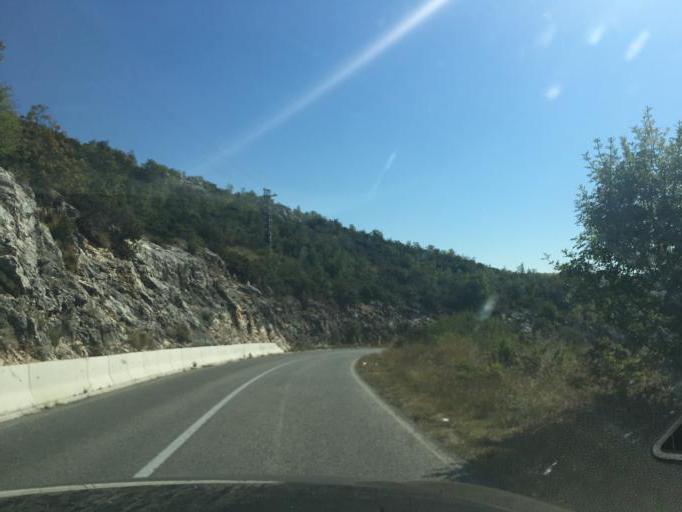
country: HR
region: Splitsko-Dalmatinska
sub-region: Grad Trogir
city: Trogir
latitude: 43.5729
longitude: 16.2422
